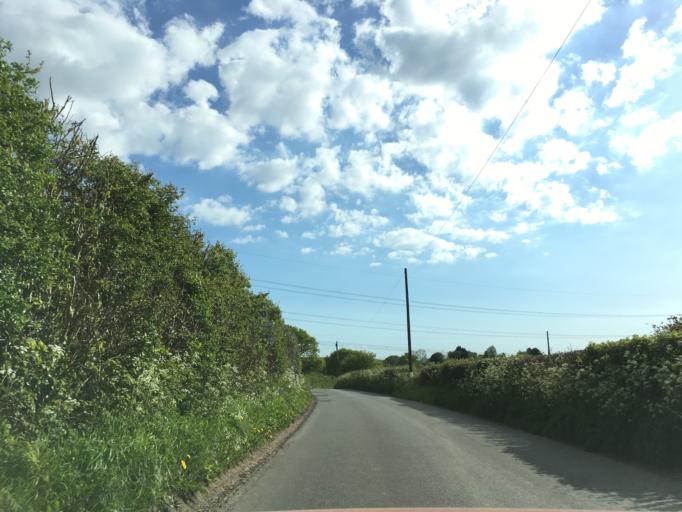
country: GB
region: Wales
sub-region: Newport
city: Marshfield
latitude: 51.5629
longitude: -3.0660
